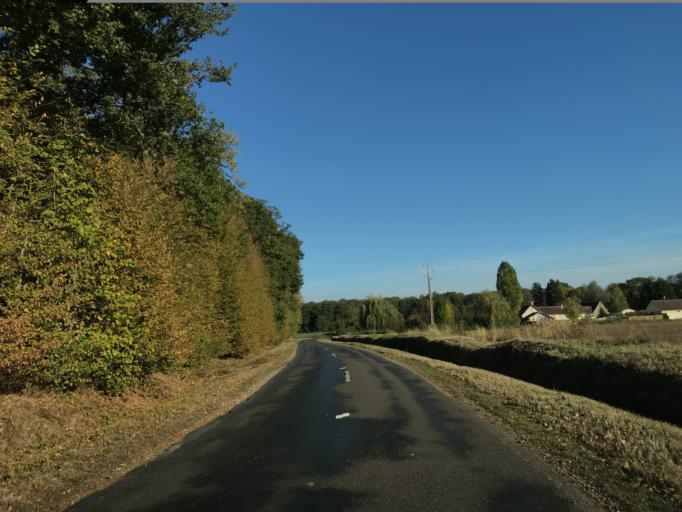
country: FR
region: Haute-Normandie
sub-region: Departement de l'Eure
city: Gravigny
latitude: 49.0769
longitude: 1.2616
